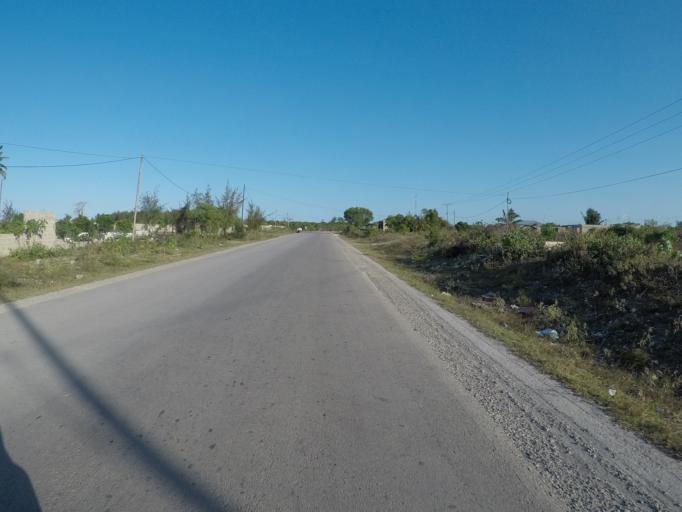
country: TZ
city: Kiwengwa
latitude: -6.1534
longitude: 39.5174
